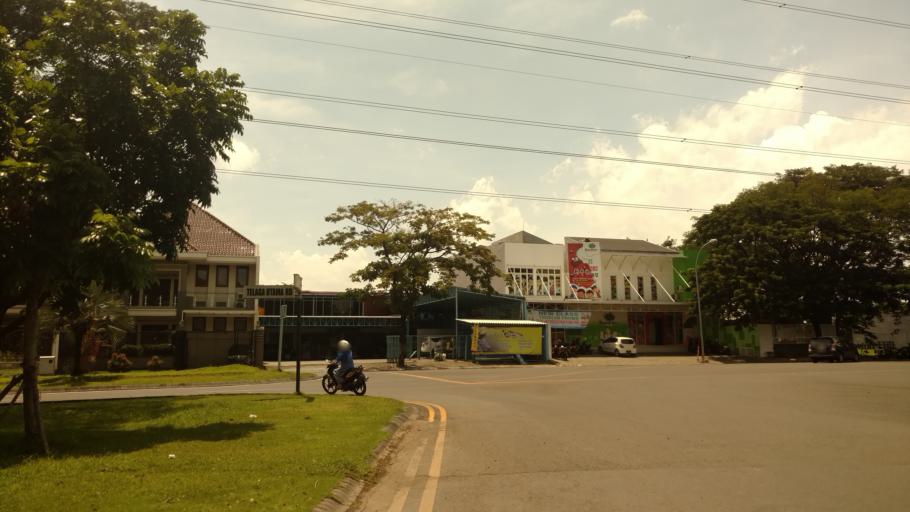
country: ID
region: East Java
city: Driyorejo
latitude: -7.2937
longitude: 112.6490
